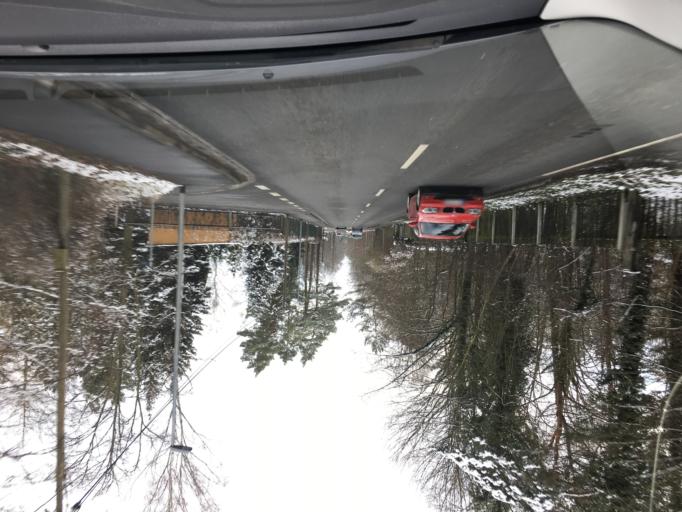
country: DE
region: Saxony
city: Brandis
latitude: 51.3097
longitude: 12.5989
